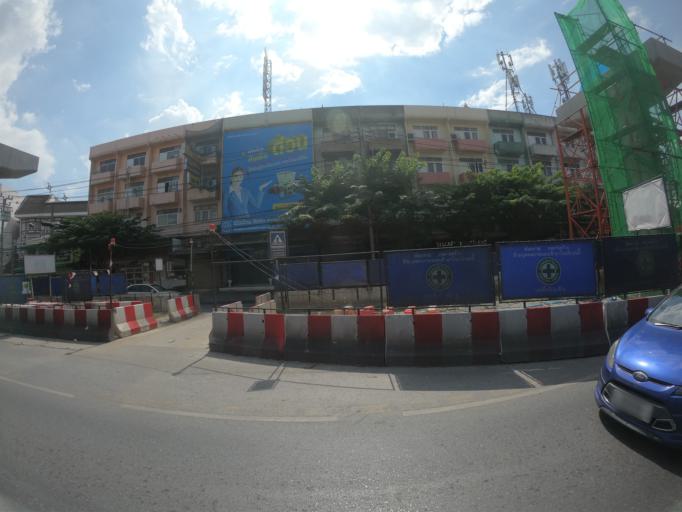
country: TH
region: Bangkok
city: Wang Thonglang
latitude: 13.7898
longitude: 100.6027
